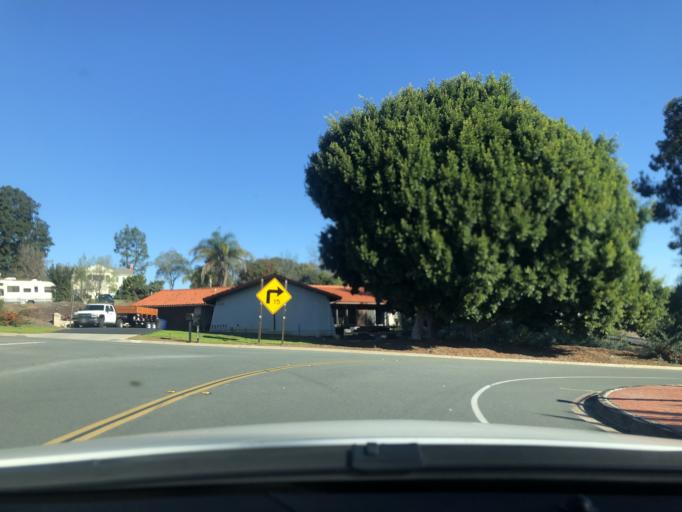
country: US
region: California
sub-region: San Diego County
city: Rancho San Diego
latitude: 32.7691
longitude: -116.9408
